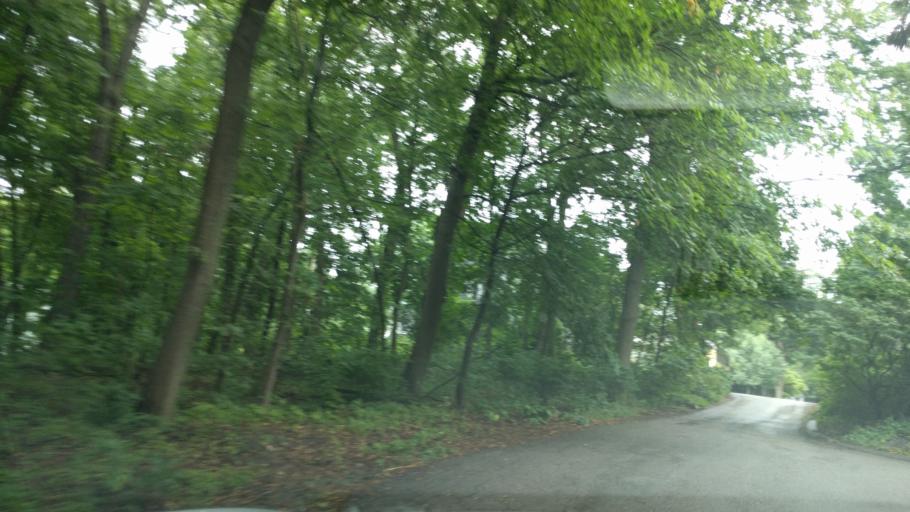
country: US
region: Massachusetts
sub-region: Worcester County
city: Worcester
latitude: 42.2838
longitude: -71.8131
